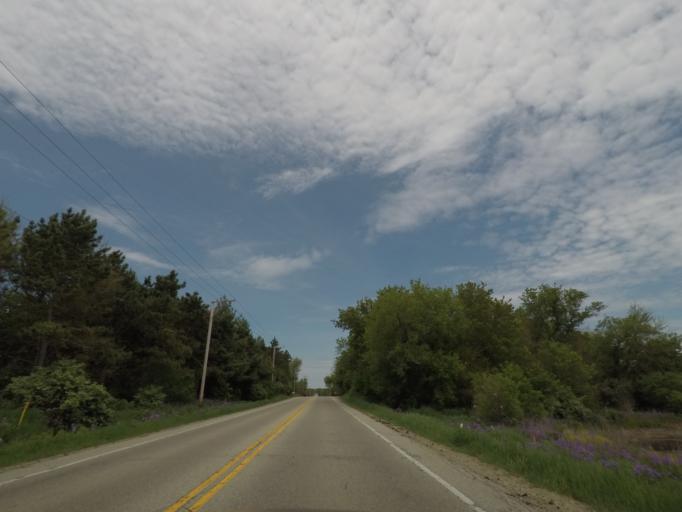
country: US
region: Wisconsin
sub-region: Green County
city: Brooklyn
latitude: 42.8761
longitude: -89.3501
